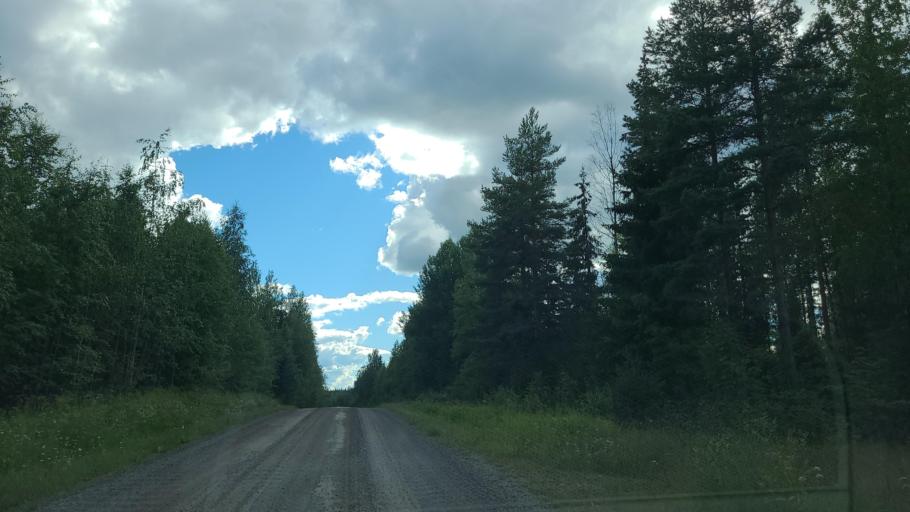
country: FI
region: Central Finland
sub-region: Jaemsae
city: Jaemsae
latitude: 61.9266
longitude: 25.3201
